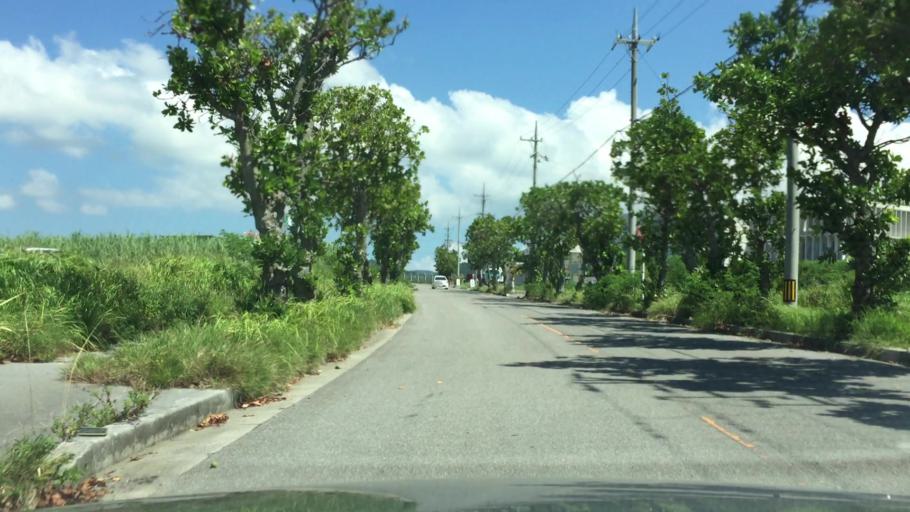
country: JP
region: Okinawa
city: Ishigaki
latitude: 24.3874
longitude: 124.2438
